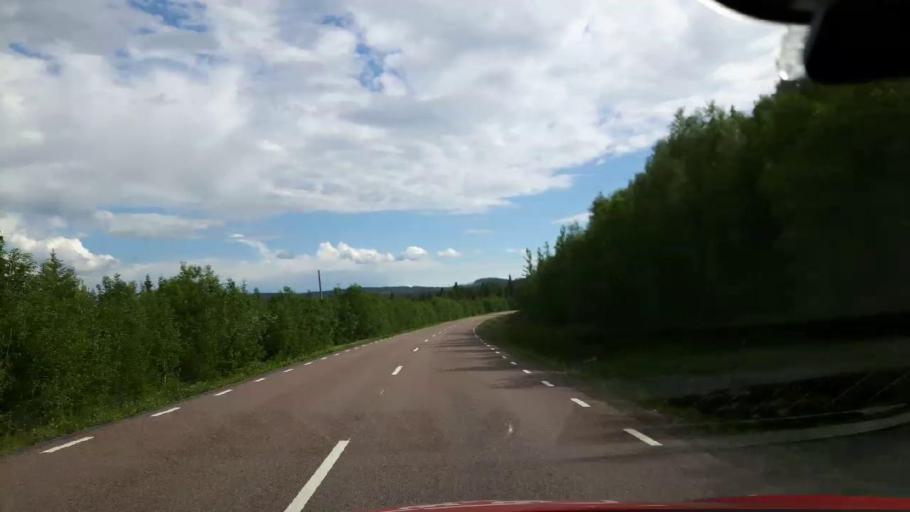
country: SE
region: Jaemtland
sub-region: Krokoms Kommun
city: Valla
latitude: 63.9245
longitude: 14.2140
